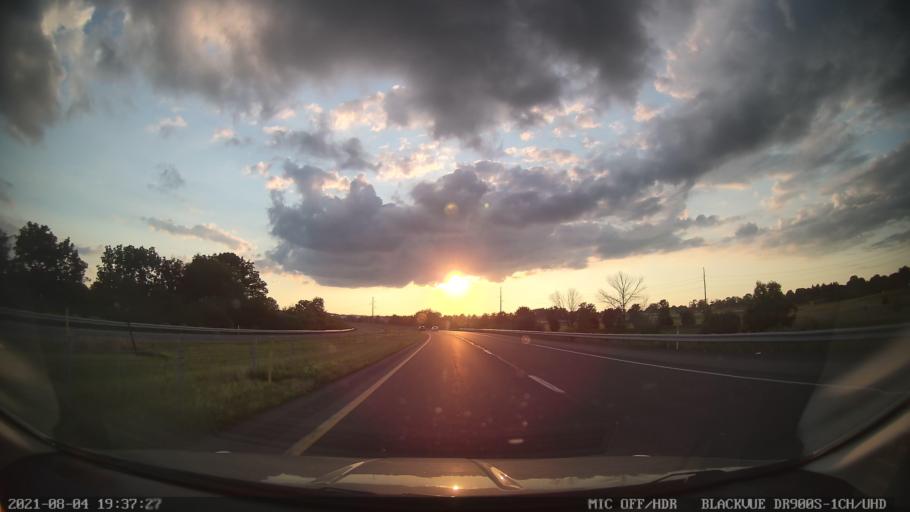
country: US
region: Pennsylvania
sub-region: Lehigh County
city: Ancient Oaks
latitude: 40.5648
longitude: -75.5891
